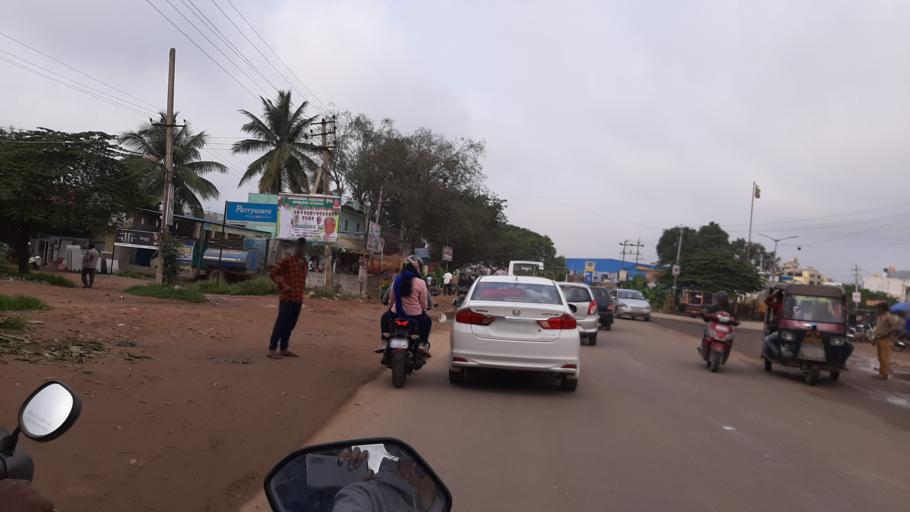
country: IN
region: Karnataka
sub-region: Bangalore Rural
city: Nelamangala
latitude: 12.9891
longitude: 77.4497
